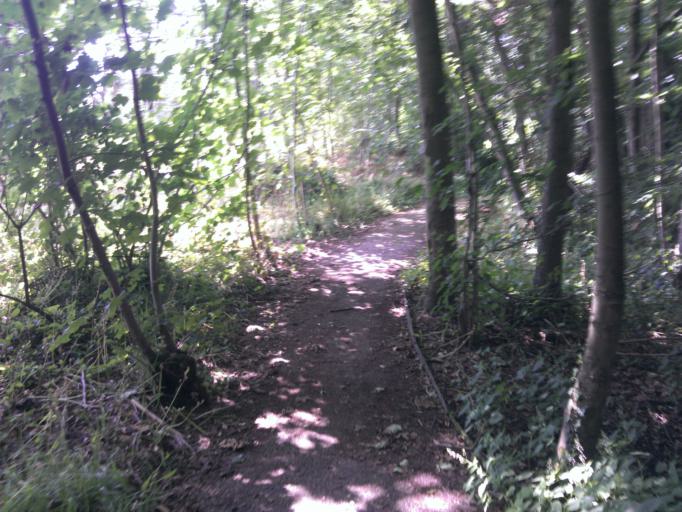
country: GB
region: England
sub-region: Essex
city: Wivenhoe
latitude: 51.8624
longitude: 0.9542
